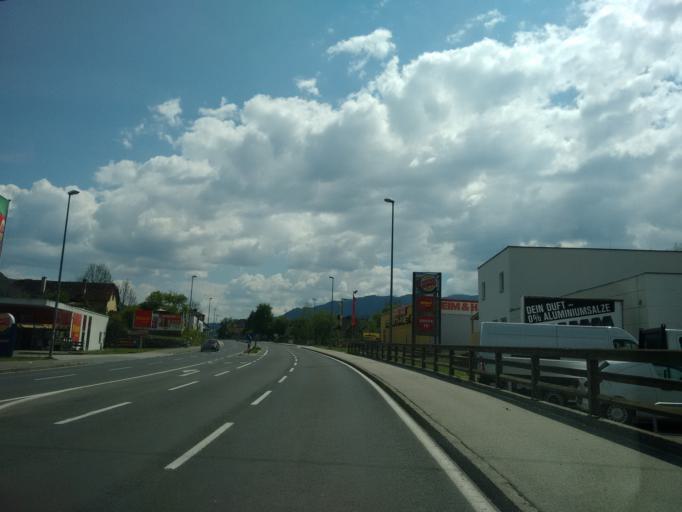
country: AT
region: Styria
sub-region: Politischer Bezirk Bruck-Muerzzuschlag
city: Bruck an der Mur
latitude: 47.4289
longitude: 15.2681
